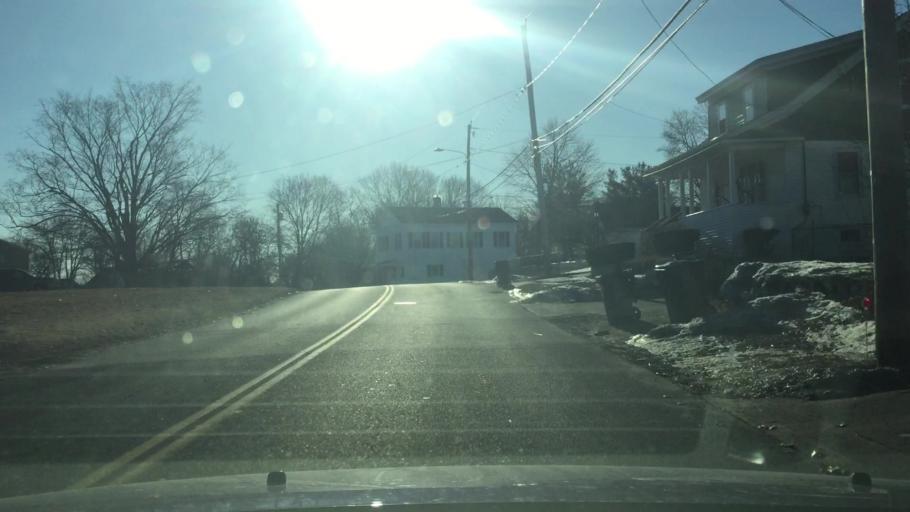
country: US
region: Massachusetts
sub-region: Middlesex County
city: Dracut
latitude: 42.6631
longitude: -71.3291
